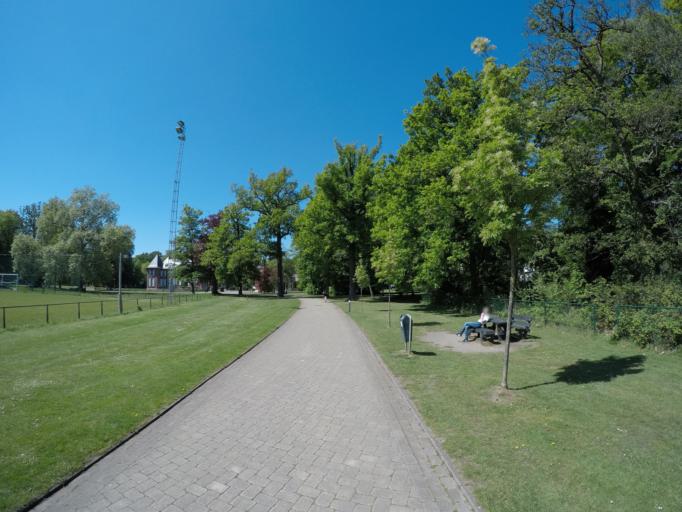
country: BE
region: Flanders
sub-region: Provincie Antwerpen
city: Schoten
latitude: 51.2448
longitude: 4.4912
